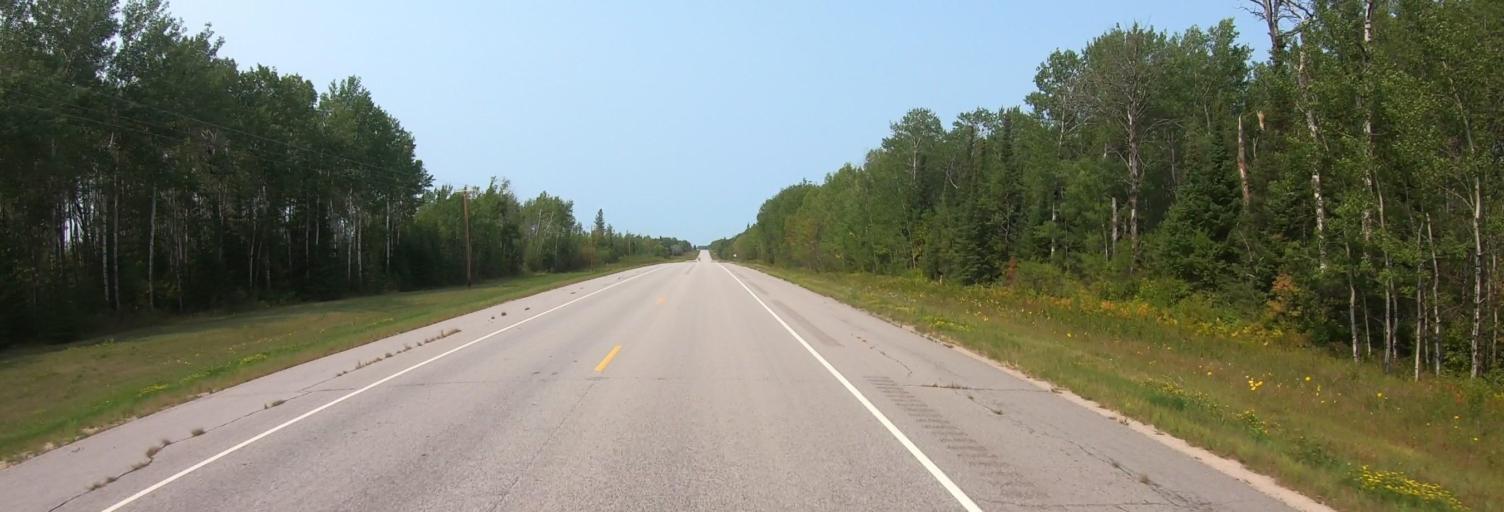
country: CA
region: Ontario
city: Fort Frances
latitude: 48.4091
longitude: -93.0969
